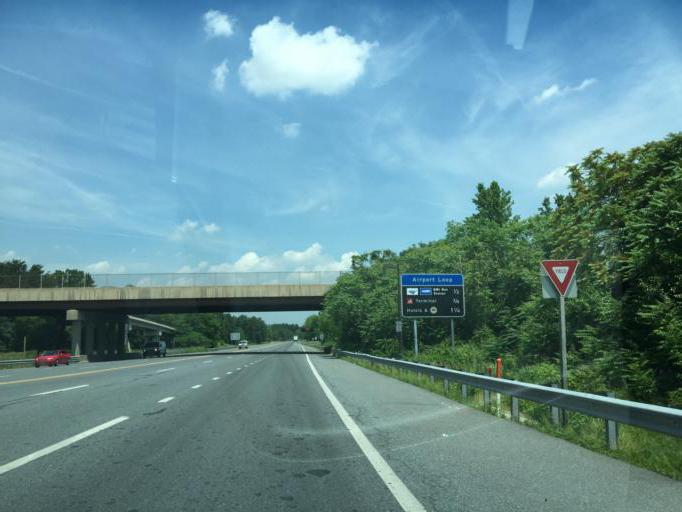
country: US
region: Maryland
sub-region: Howard County
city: Hanover
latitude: 39.1772
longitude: -76.6929
